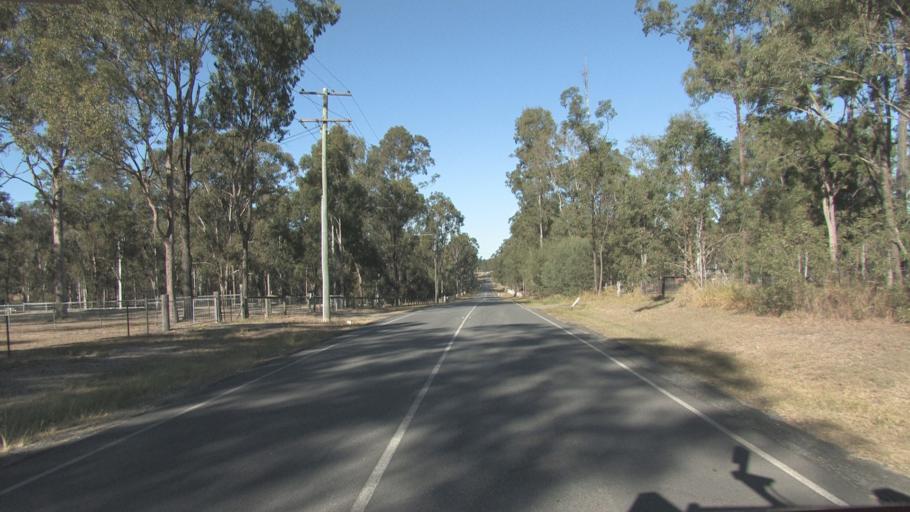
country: AU
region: Queensland
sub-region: Logan
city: North Maclean
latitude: -27.8156
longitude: 152.9886
